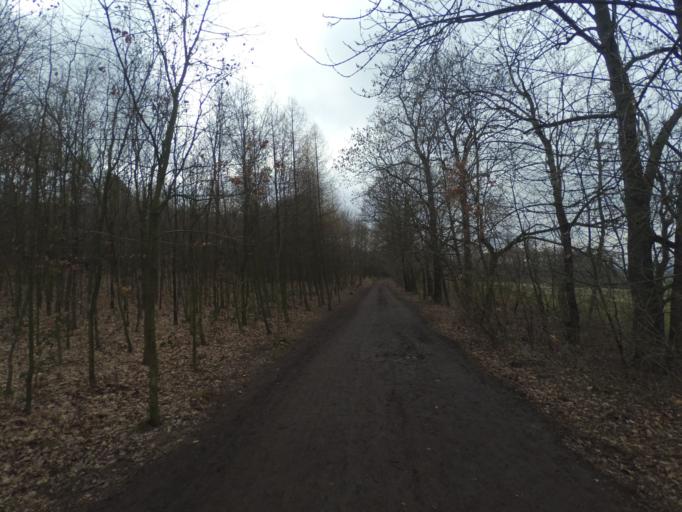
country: CZ
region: Praha
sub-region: Praha 9
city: Strizkov
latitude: 50.1389
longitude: 14.4686
